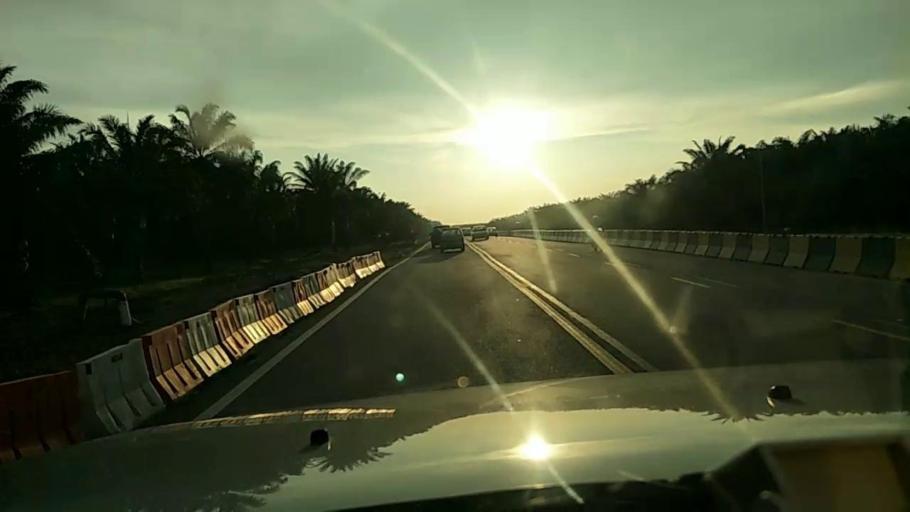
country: MY
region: Perak
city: Kampong Dungun
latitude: 3.3066
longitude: 101.3434
